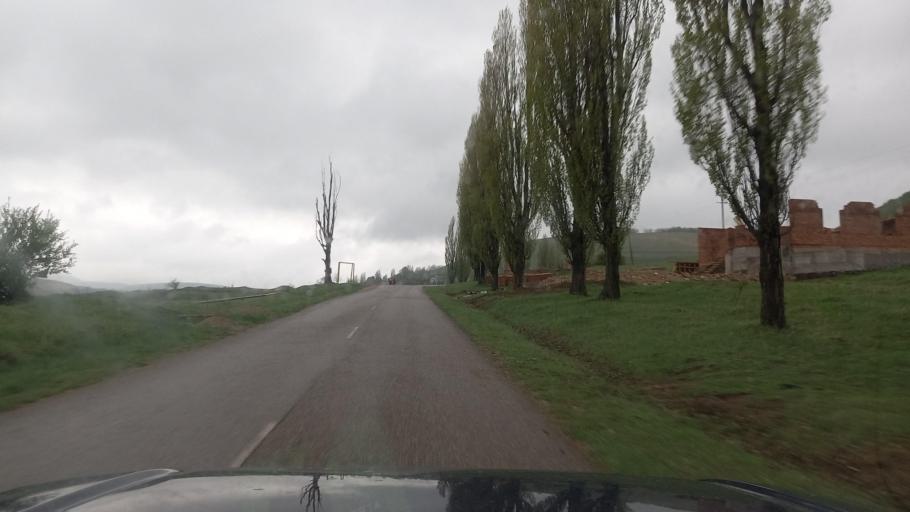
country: RU
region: Stavropol'skiy
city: Nezhinskiy
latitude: 43.8745
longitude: 42.6731
